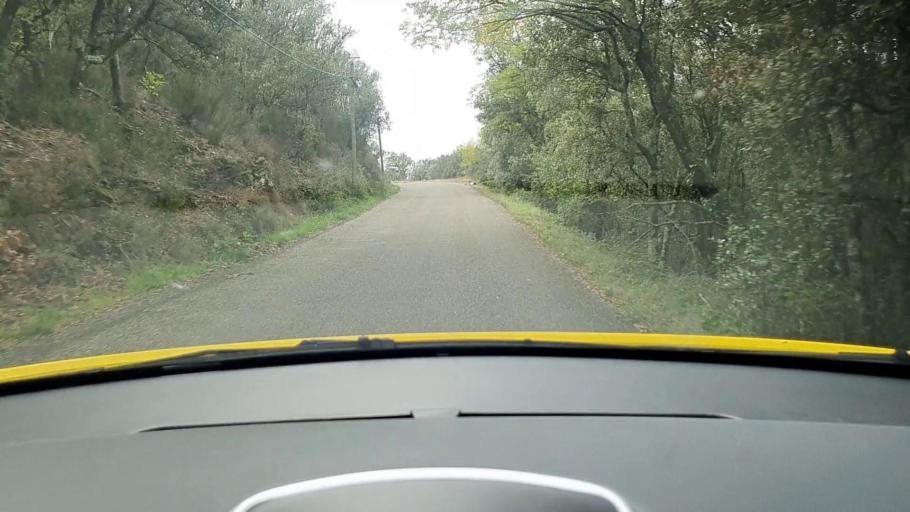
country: FR
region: Languedoc-Roussillon
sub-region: Departement du Gard
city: Sumene
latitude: 44.0173
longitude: 3.6617
